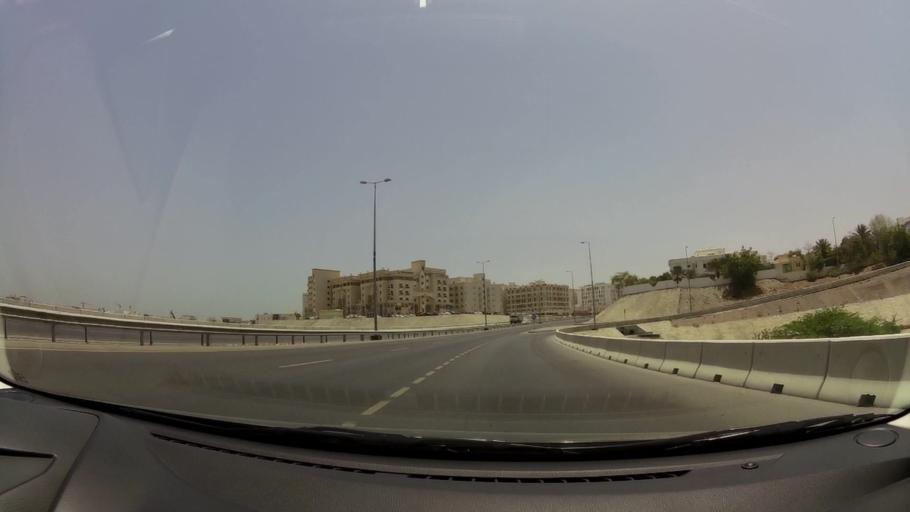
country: OM
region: Muhafazat Masqat
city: Bawshar
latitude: 23.5842
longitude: 58.4205
